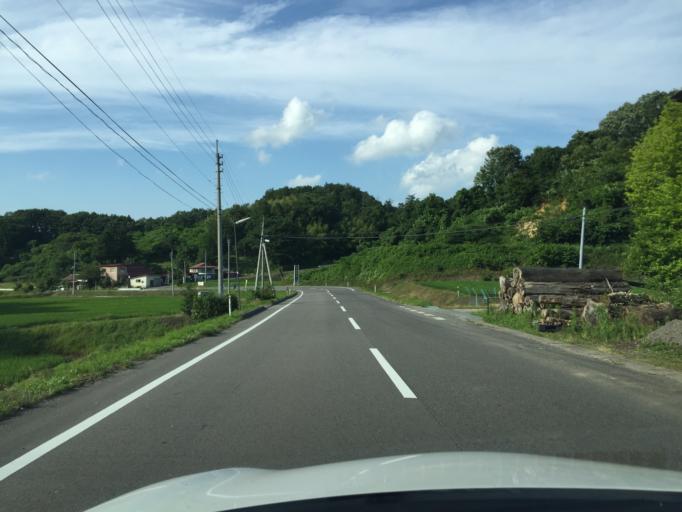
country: JP
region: Fukushima
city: Miharu
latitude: 37.3700
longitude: 140.5137
